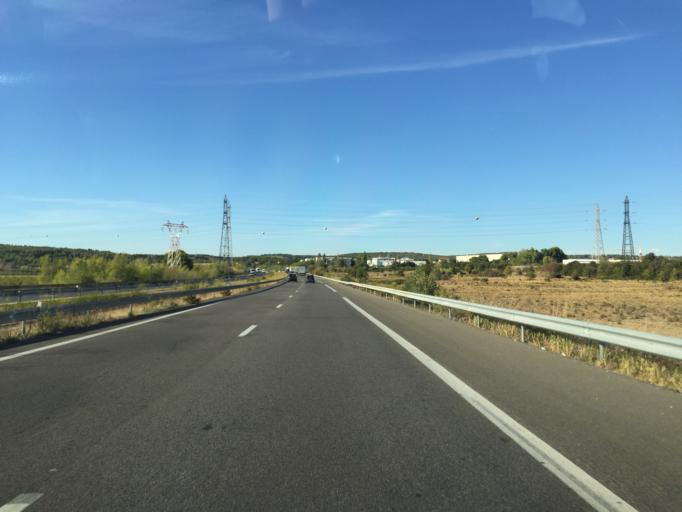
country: FR
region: Provence-Alpes-Cote d'Azur
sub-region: Departement des Bouches-du-Rhone
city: Rognac
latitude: 43.5074
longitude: 5.2364
